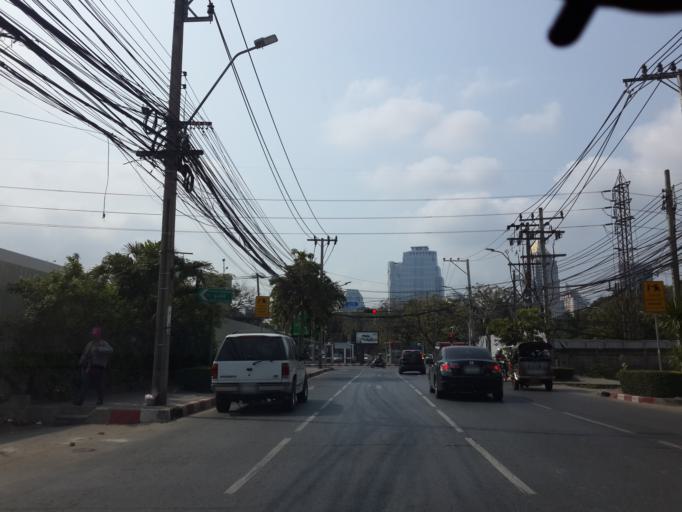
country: TH
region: Bangkok
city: Pathum Wan
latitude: 13.7350
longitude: 100.5423
